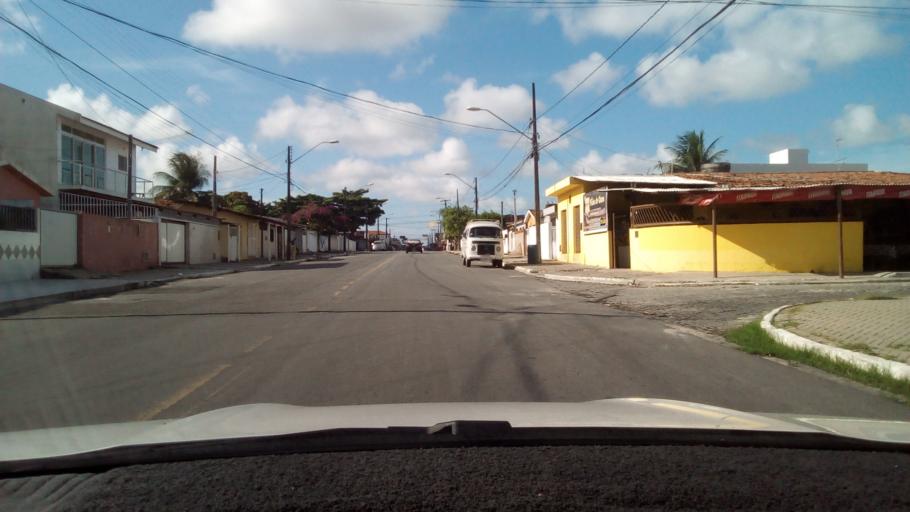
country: BR
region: Paraiba
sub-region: Joao Pessoa
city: Joao Pessoa
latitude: -7.1865
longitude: -34.8433
